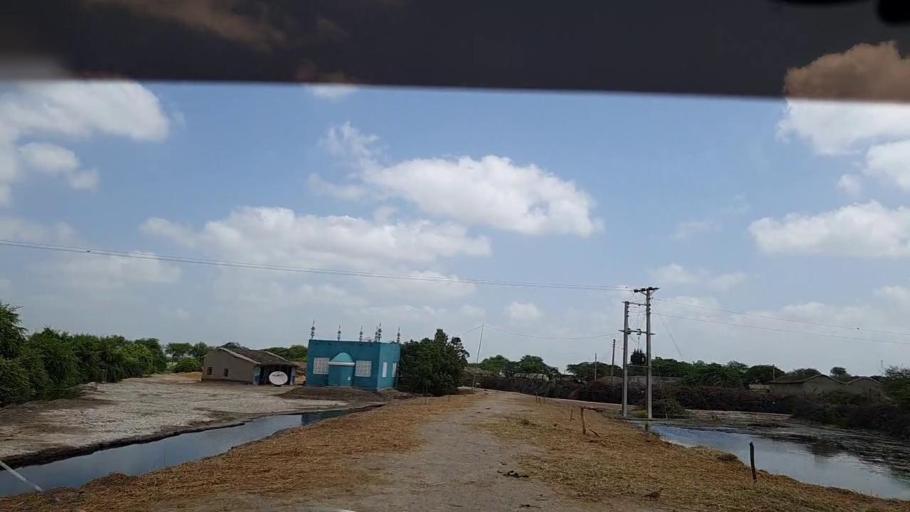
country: PK
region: Sindh
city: Badin
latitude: 24.5836
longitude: 68.7670
